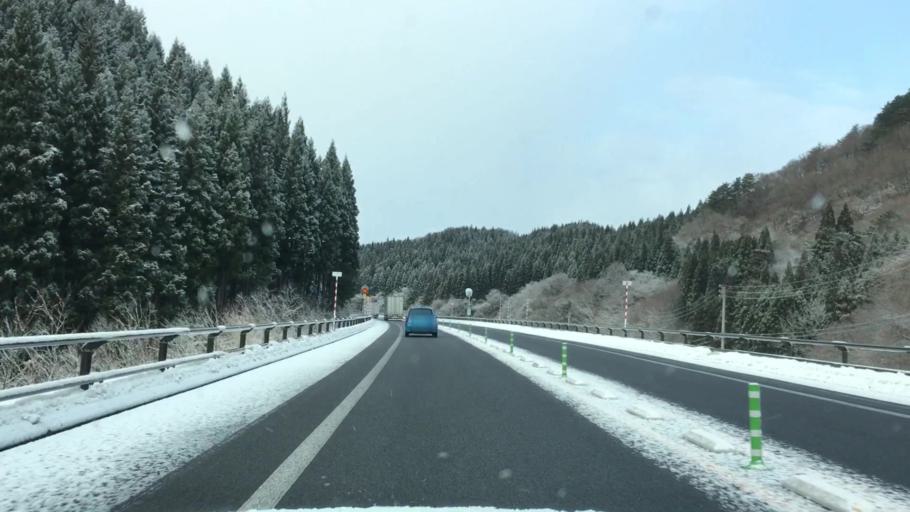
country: JP
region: Akita
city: Takanosu
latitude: 40.2263
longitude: 140.4464
